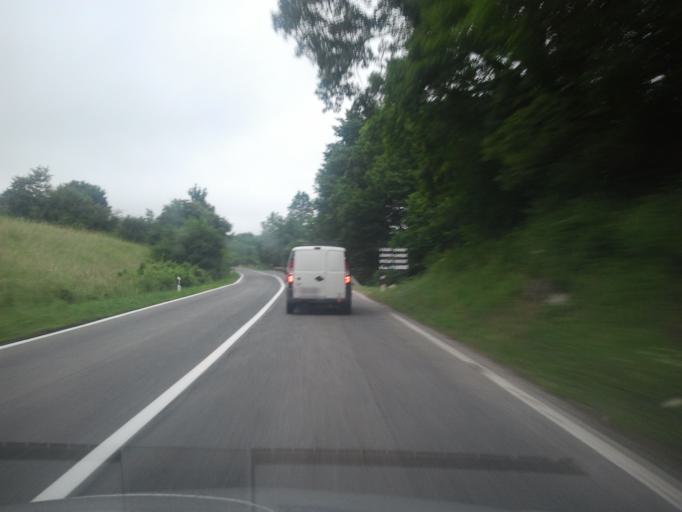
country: HR
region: Karlovacka
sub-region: Grad Karlovac
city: Slunj
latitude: 45.1364
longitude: 15.5603
